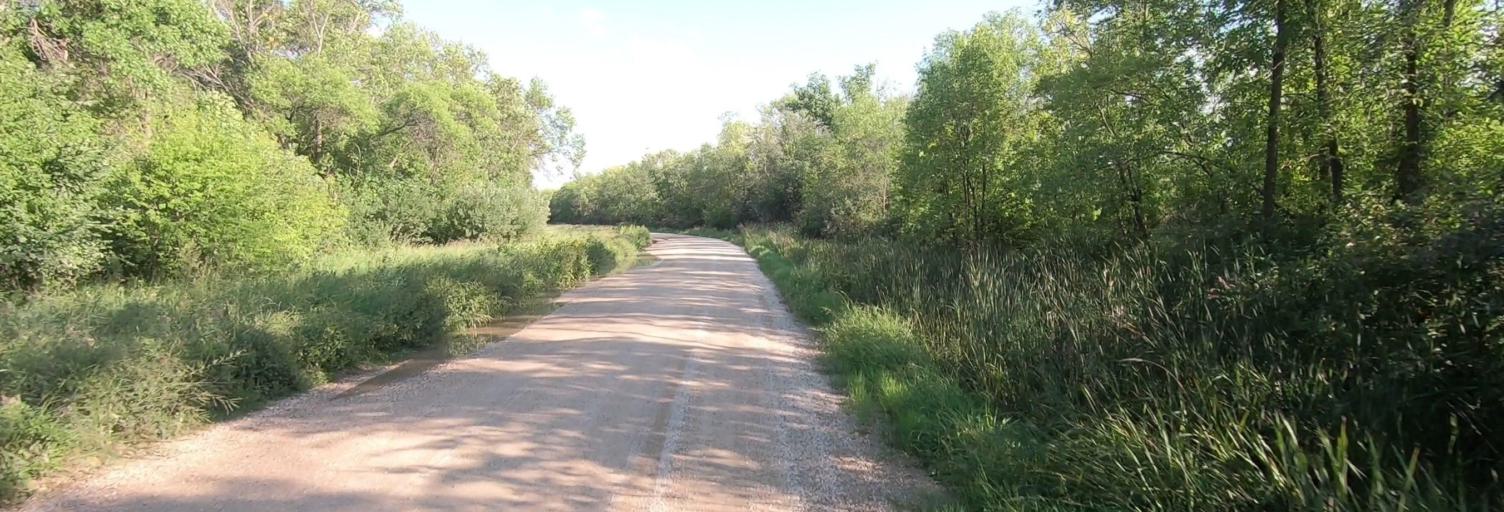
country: CA
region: Manitoba
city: Selkirk
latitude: 50.2865
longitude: -96.8638
